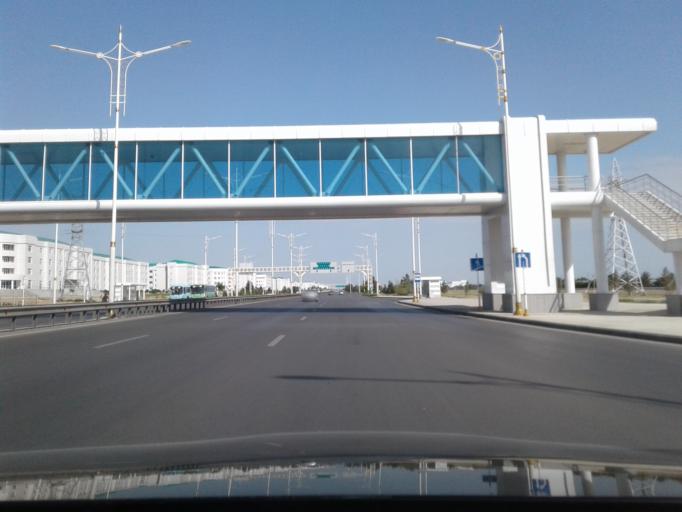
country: TM
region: Ahal
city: Ashgabat
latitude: 37.9800
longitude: 58.3388
